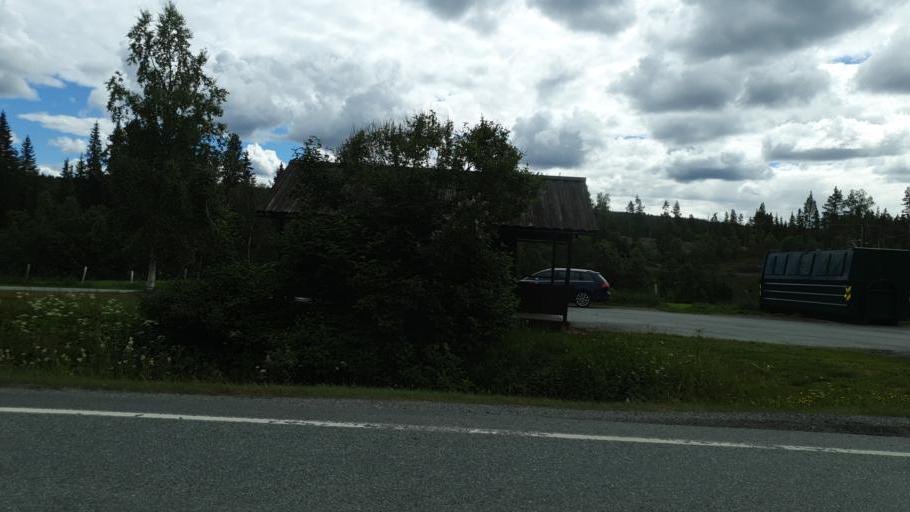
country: NO
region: Sor-Trondelag
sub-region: Rennebu
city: Berkak
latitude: 62.9035
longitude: 10.1160
